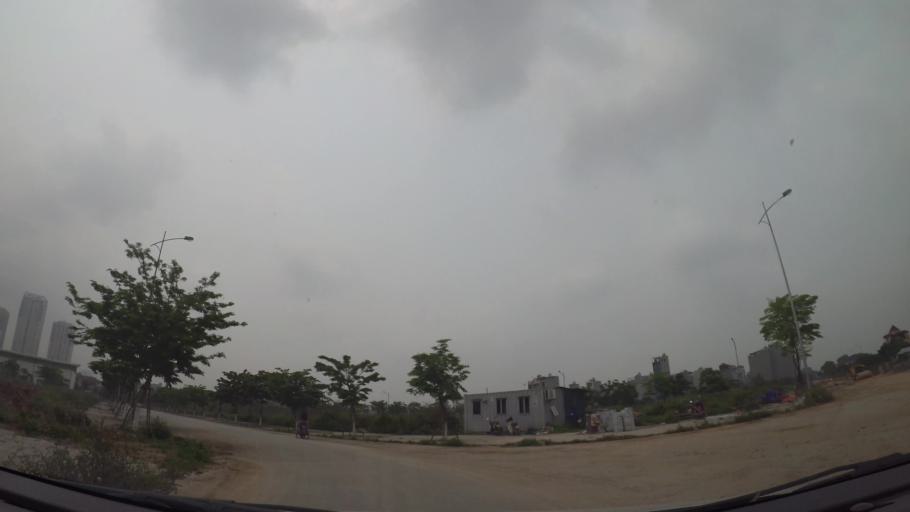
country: VN
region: Ha Noi
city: Ha Dong
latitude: 20.9776
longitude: 105.7506
